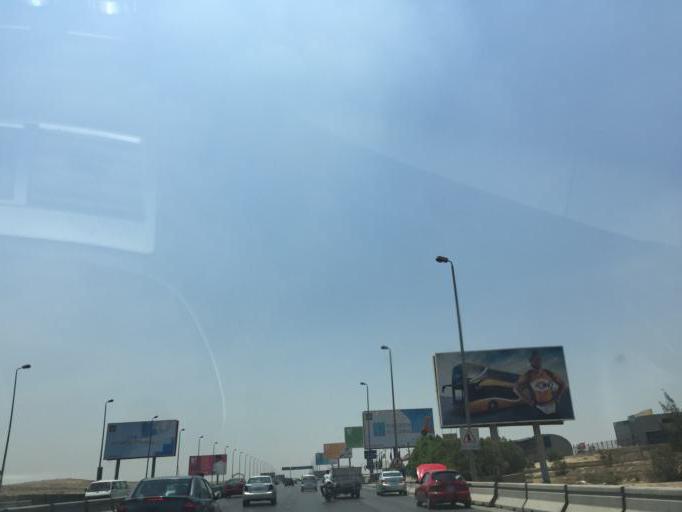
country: EG
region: Al Jizah
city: Awsim
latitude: 30.0538
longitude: 31.0688
